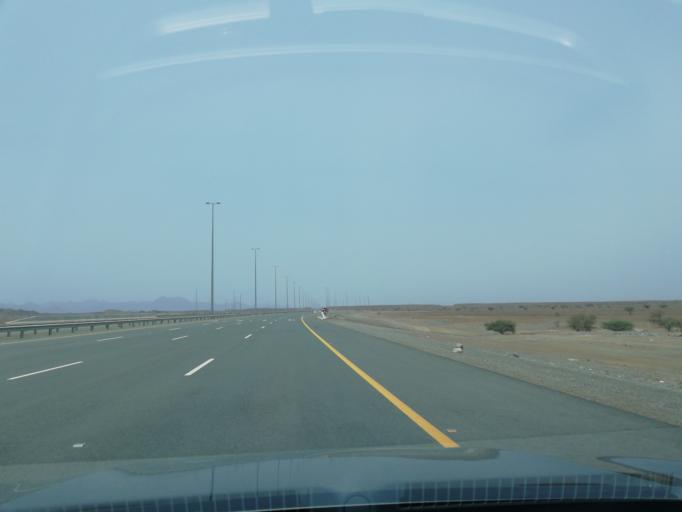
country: OM
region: Al Batinah
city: Al Liwa'
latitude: 24.5598
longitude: 56.4679
